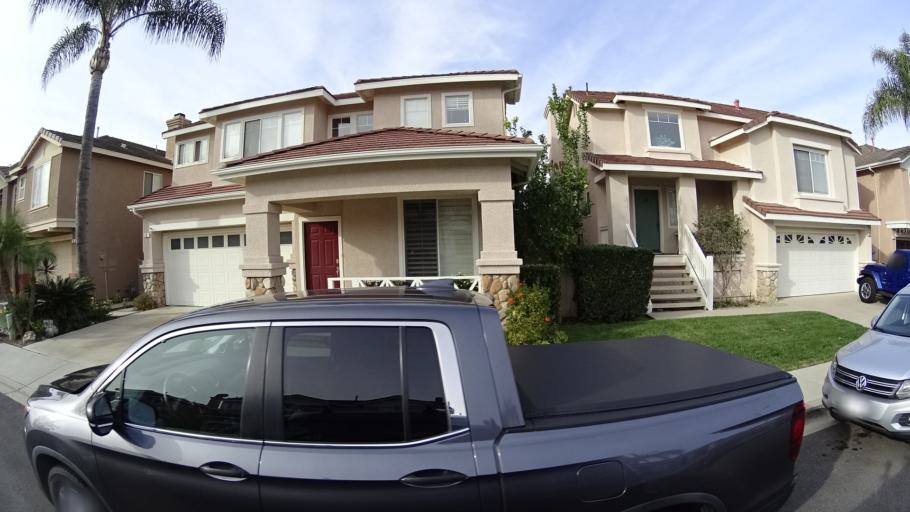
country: US
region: California
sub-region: Orange County
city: Aliso Viejo
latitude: 33.5606
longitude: -117.7318
